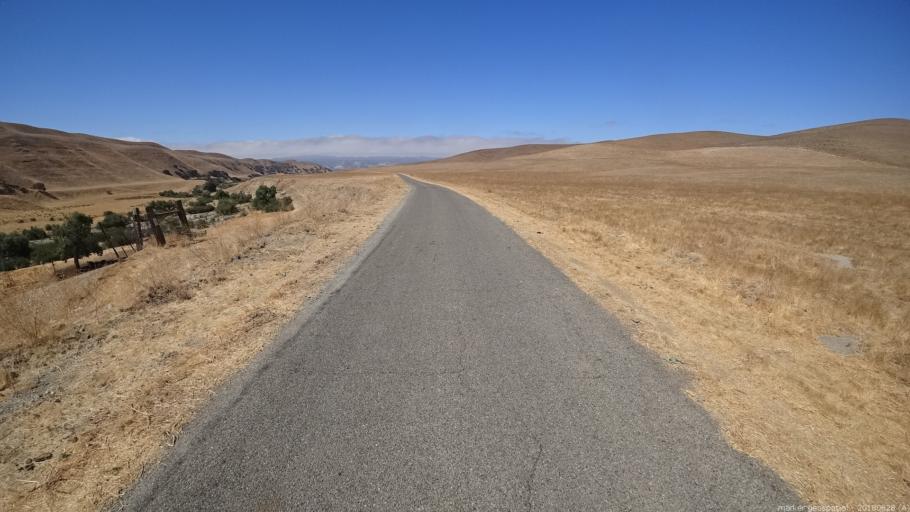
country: US
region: California
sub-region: San Luis Obispo County
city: Lake Nacimiento
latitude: 36.0405
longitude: -120.8365
